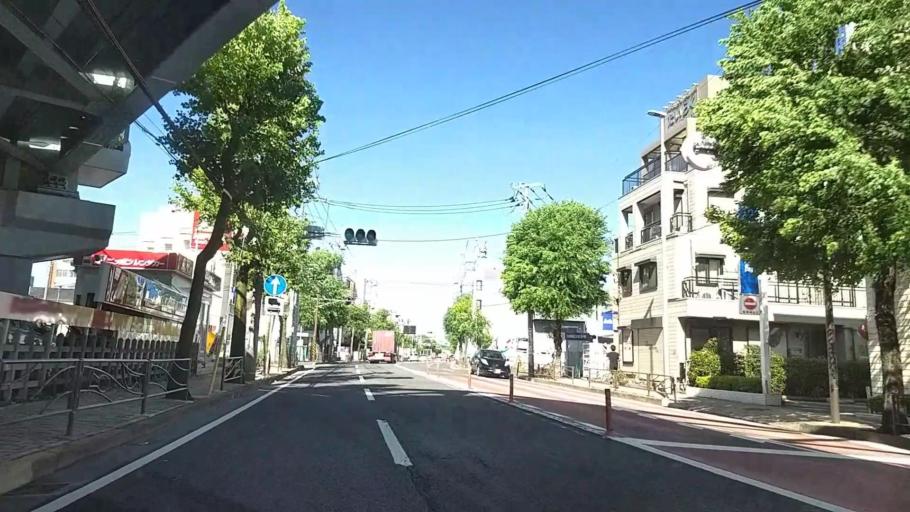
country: JP
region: Tokyo
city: Chofugaoka
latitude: 35.5847
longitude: 139.5808
